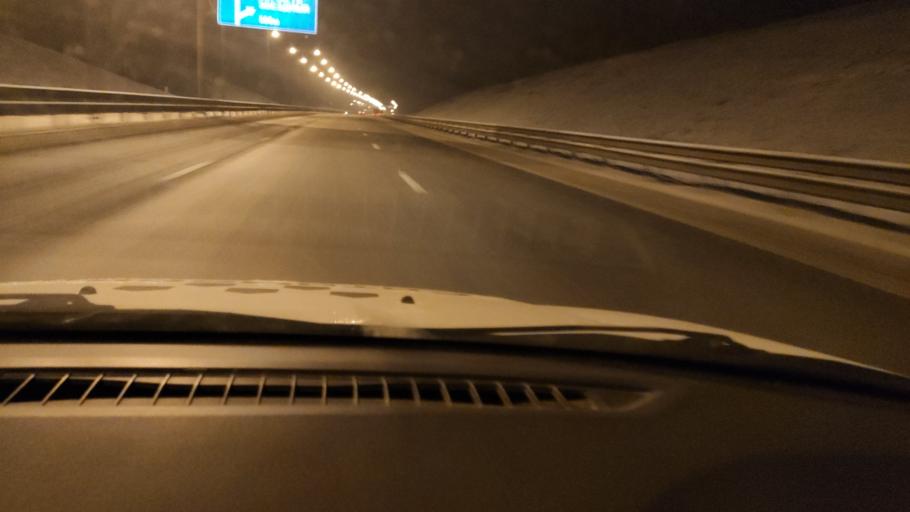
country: RU
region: Perm
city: Bershet'
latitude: 57.7275
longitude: 56.3506
